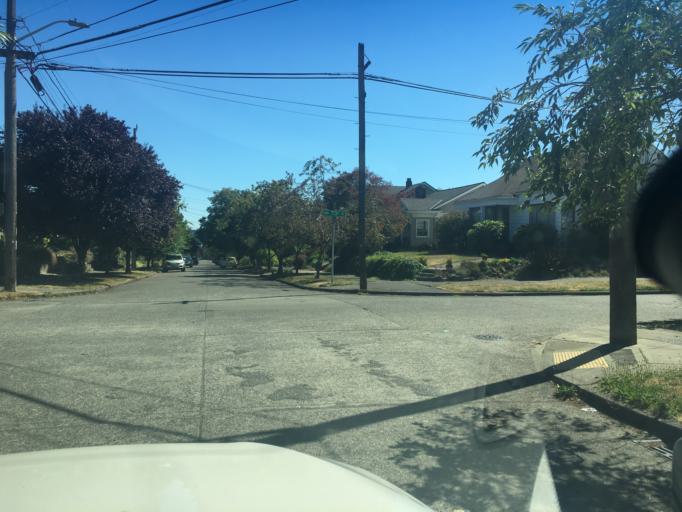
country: US
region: Washington
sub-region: King County
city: Shoreline
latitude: 47.6815
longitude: -122.3898
